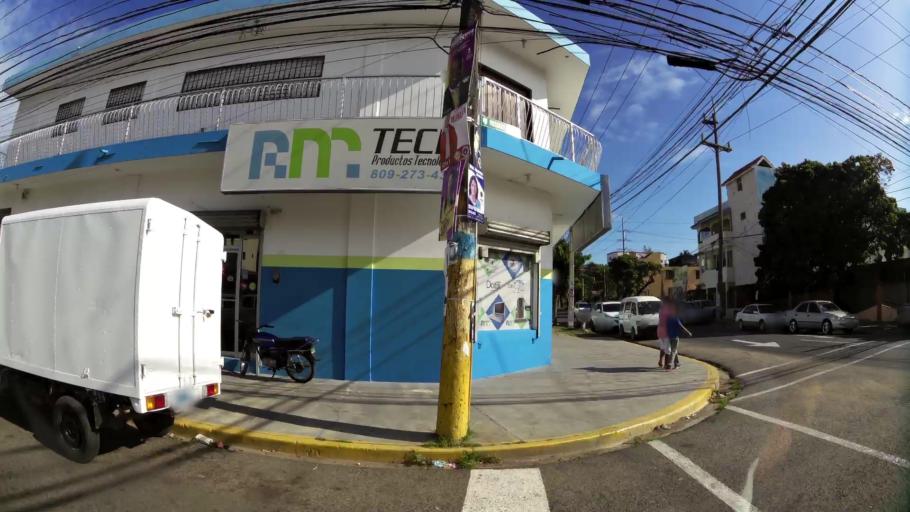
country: DO
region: Santo Domingo
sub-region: Santo Domingo
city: Santo Domingo Este
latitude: 18.4890
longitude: -69.8766
